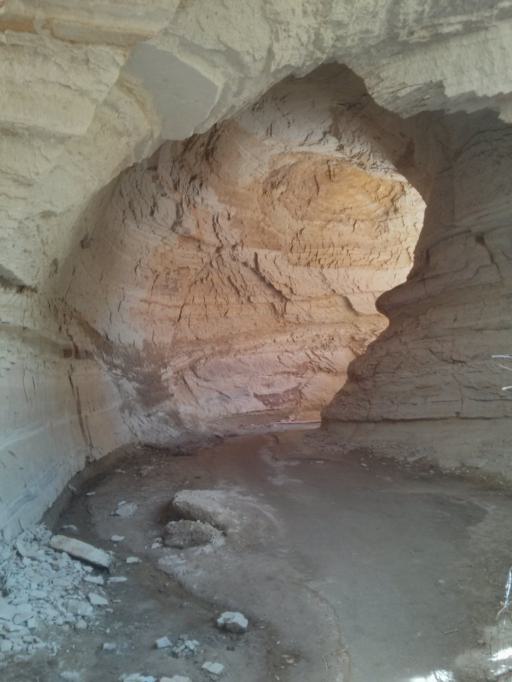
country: TR
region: Nevsehir
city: Goereme
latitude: 38.6432
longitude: 34.8537
